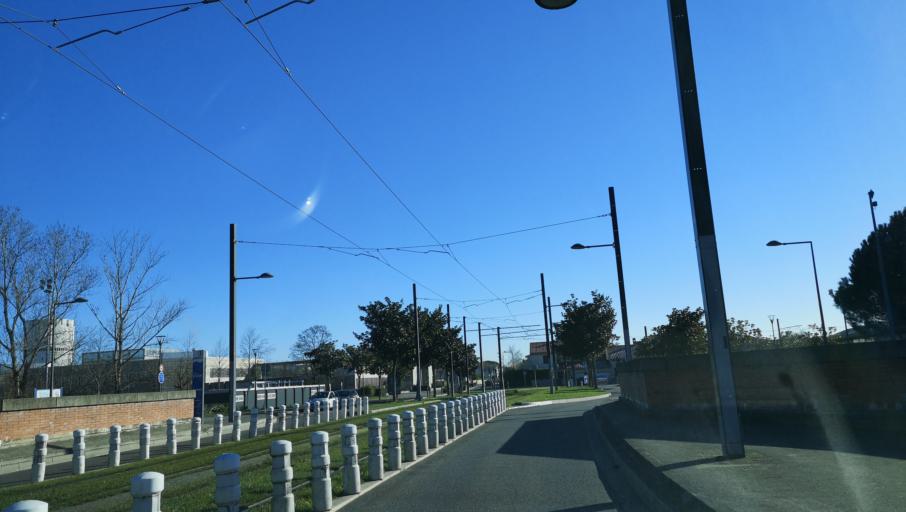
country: FR
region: Midi-Pyrenees
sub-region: Departement de la Haute-Garonne
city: Blagnac
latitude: 43.6445
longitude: 1.3779
